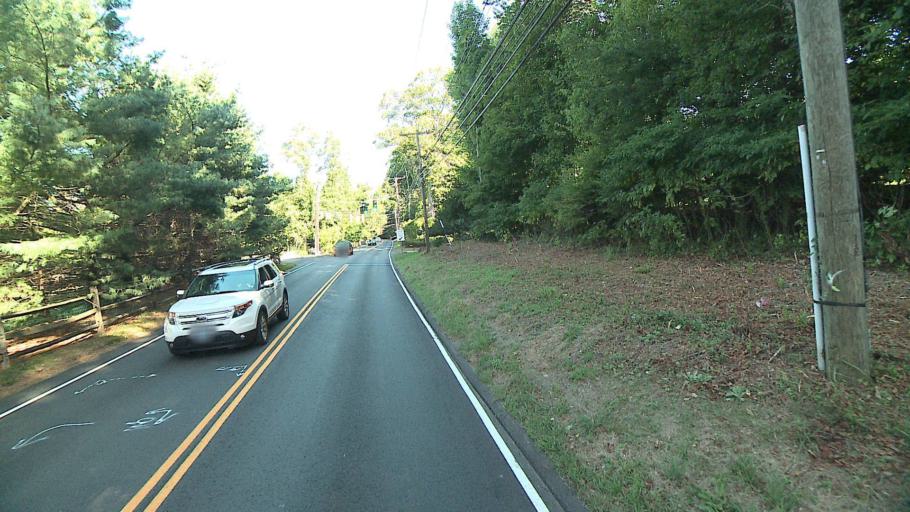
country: US
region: Connecticut
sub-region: Fairfield County
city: Darien
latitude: 41.1033
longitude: -73.4833
